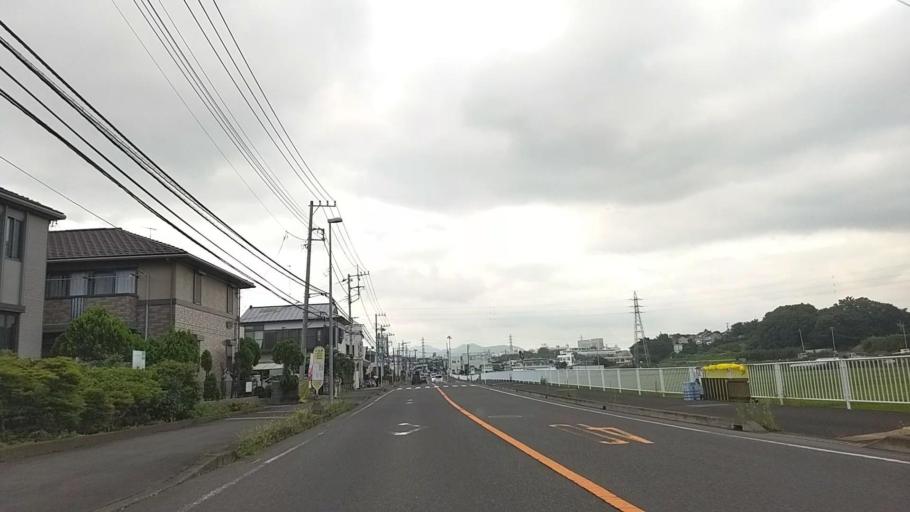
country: JP
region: Kanagawa
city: Isehara
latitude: 35.3800
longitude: 139.3175
